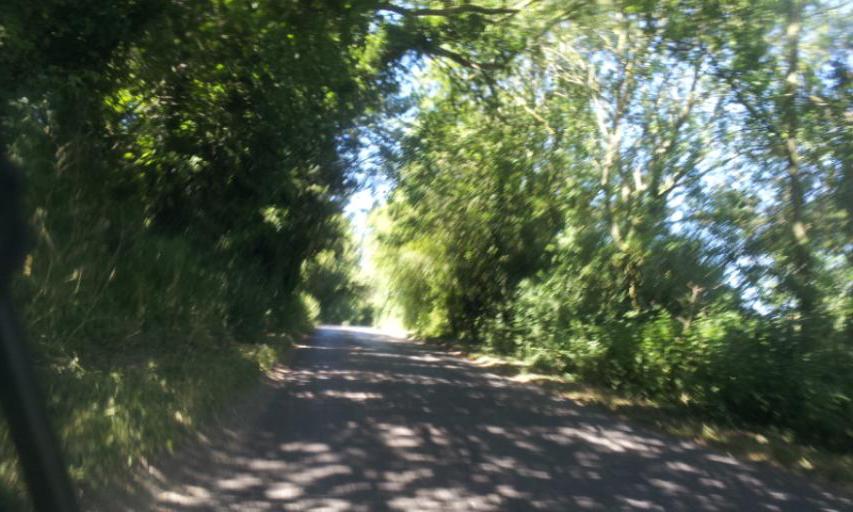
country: GB
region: England
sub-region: Kent
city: Sittingbourne
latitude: 51.3075
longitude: 0.7404
